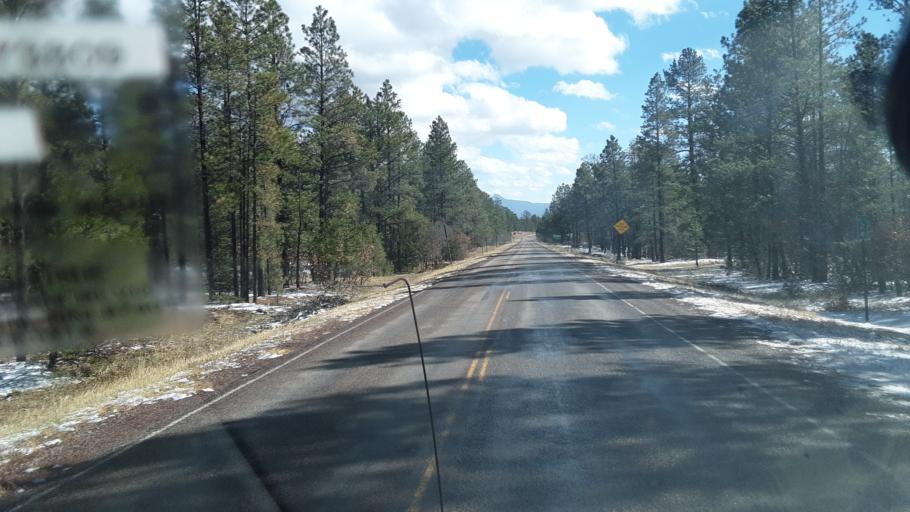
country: US
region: New Mexico
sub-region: Rio Arriba County
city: Santa Teresa
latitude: 36.1994
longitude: -106.7557
